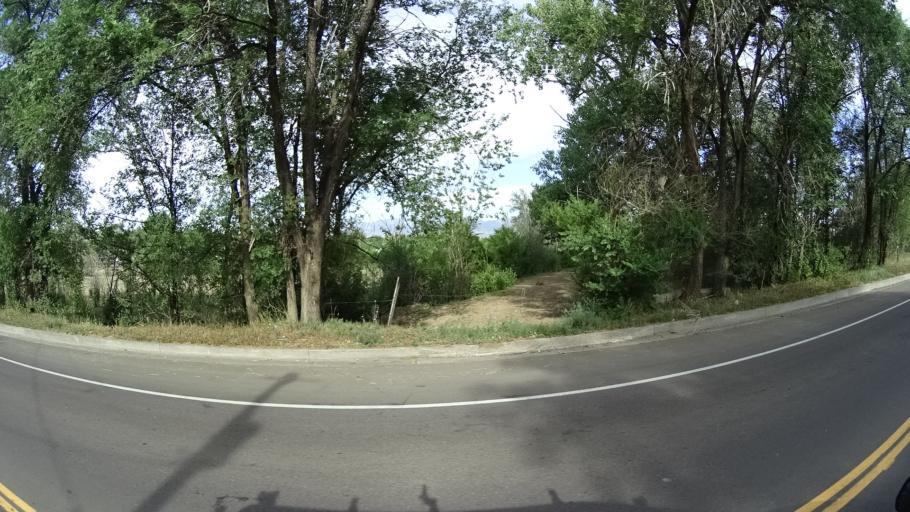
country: US
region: Colorado
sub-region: El Paso County
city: Fountain
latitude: 38.6848
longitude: -104.6943
